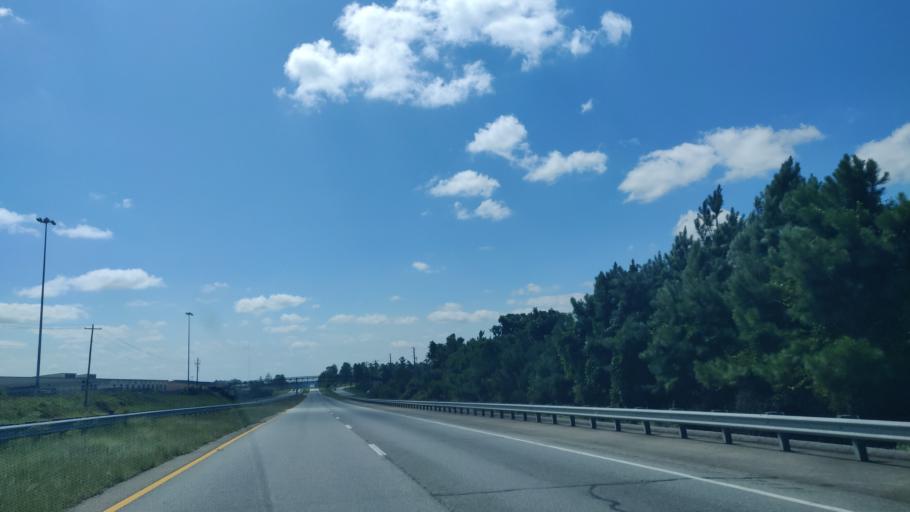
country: US
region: Georgia
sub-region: Chattahoochee County
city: Cusseta
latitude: 32.3704
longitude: -84.8557
